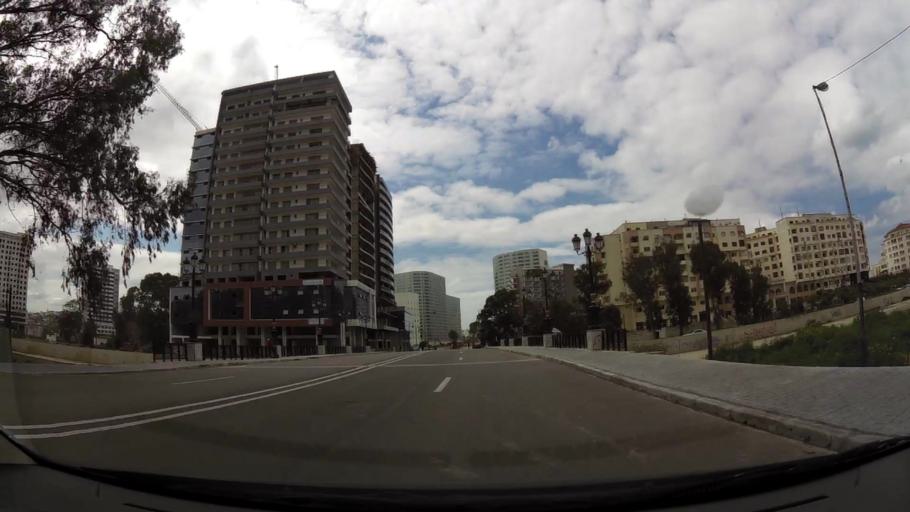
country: MA
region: Tanger-Tetouan
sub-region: Tanger-Assilah
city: Tangier
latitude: 35.7734
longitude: -5.7806
